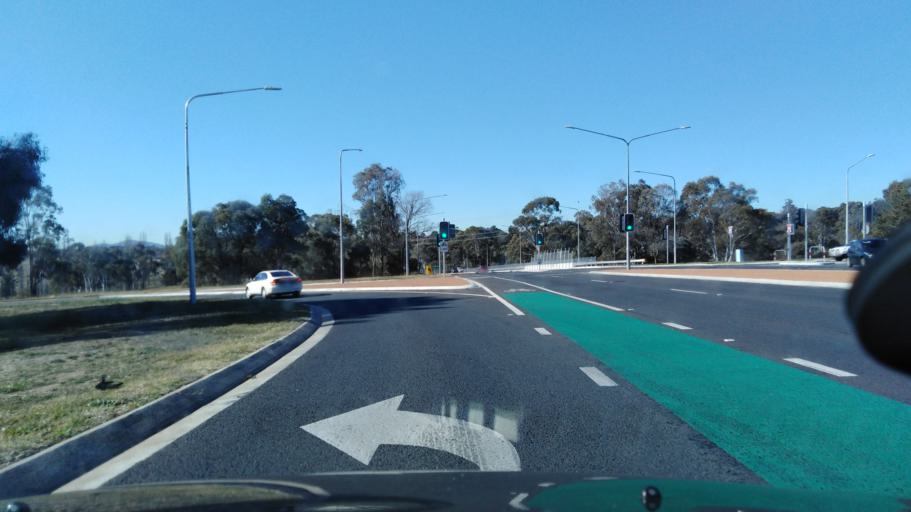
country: AU
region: Australian Capital Territory
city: Forrest
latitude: -35.3204
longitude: 149.0623
